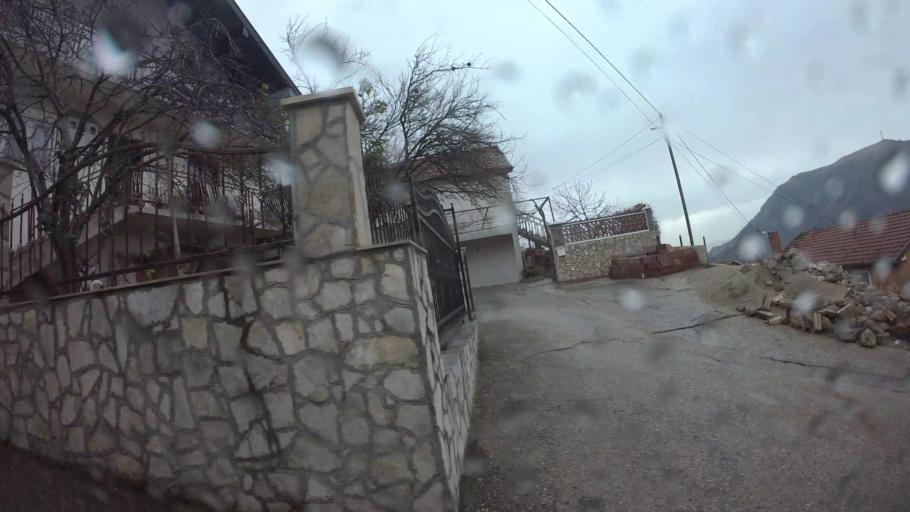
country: BA
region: Federation of Bosnia and Herzegovina
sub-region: Hercegovacko-Bosanski Kanton
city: Mostar
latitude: 43.3448
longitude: 17.8188
